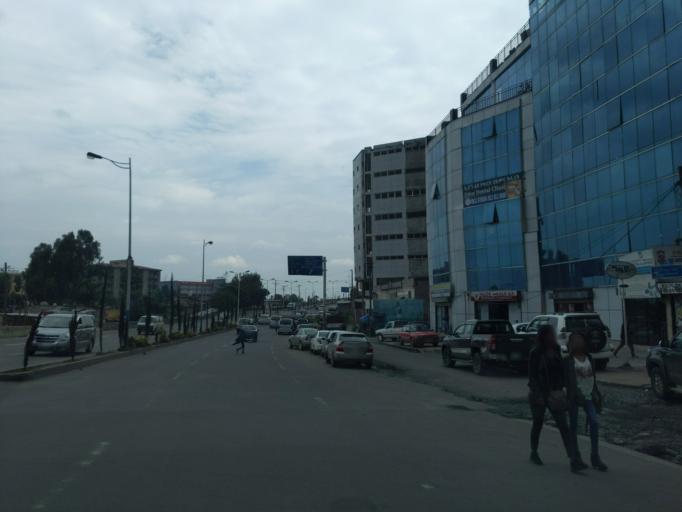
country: ET
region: Adis Abeba
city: Addis Ababa
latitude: 8.9814
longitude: 38.7632
